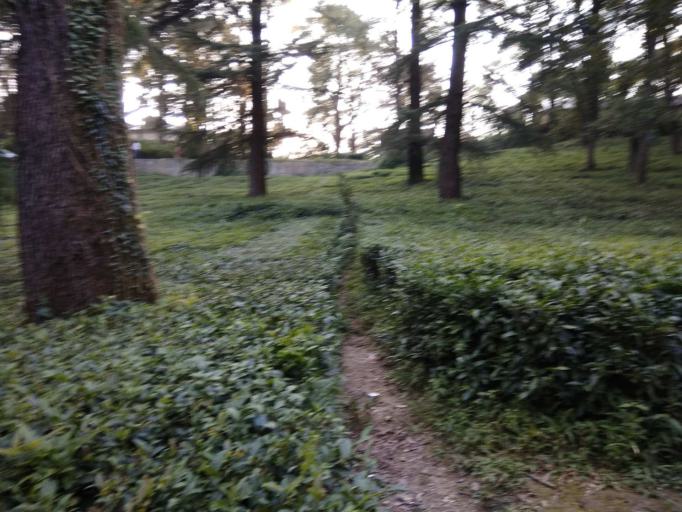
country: IN
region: Himachal Pradesh
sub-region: Kangra
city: Palampur
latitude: 32.1178
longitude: 76.5396
